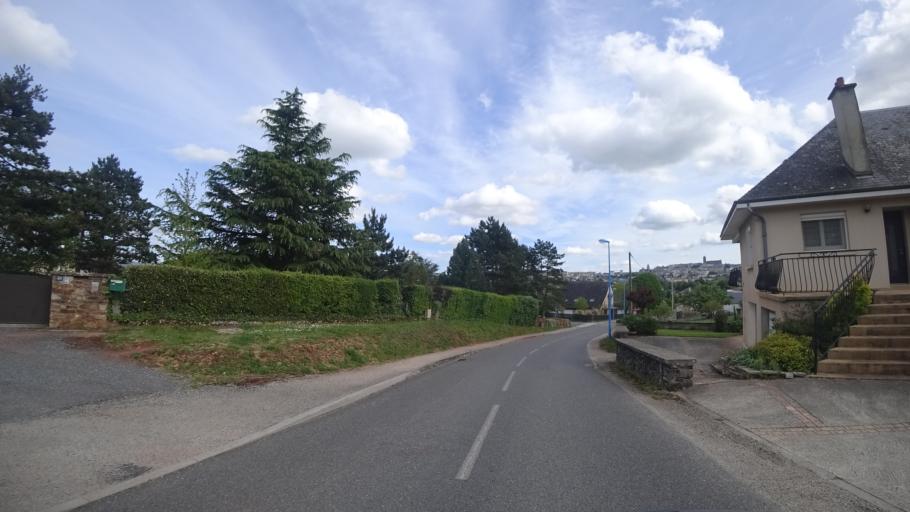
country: FR
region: Midi-Pyrenees
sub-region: Departement de l'Aveyron
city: Rodez
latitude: 44.3735
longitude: 2.5729
